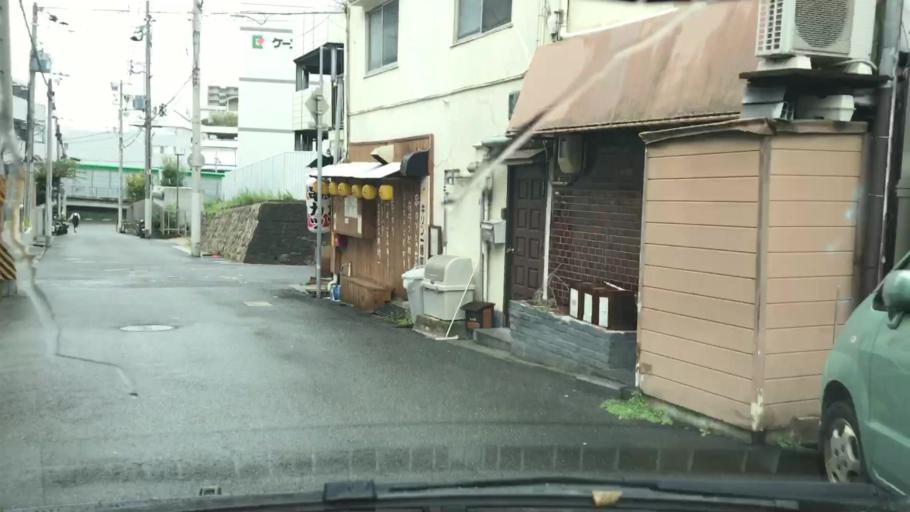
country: JP
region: Hyogo
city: Kobe
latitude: 34.7049
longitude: 135.2211
